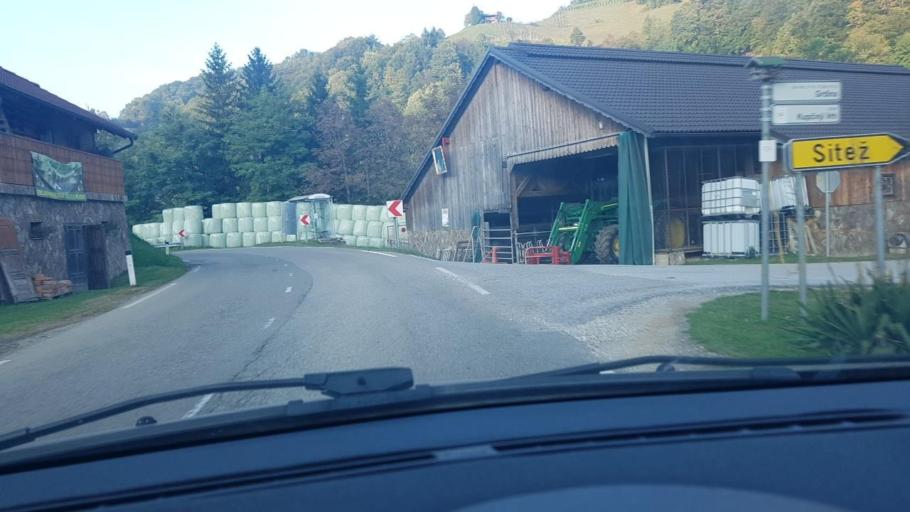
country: SI
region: Majsperk
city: Majsperk
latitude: 46.2948
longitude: 15.7212
